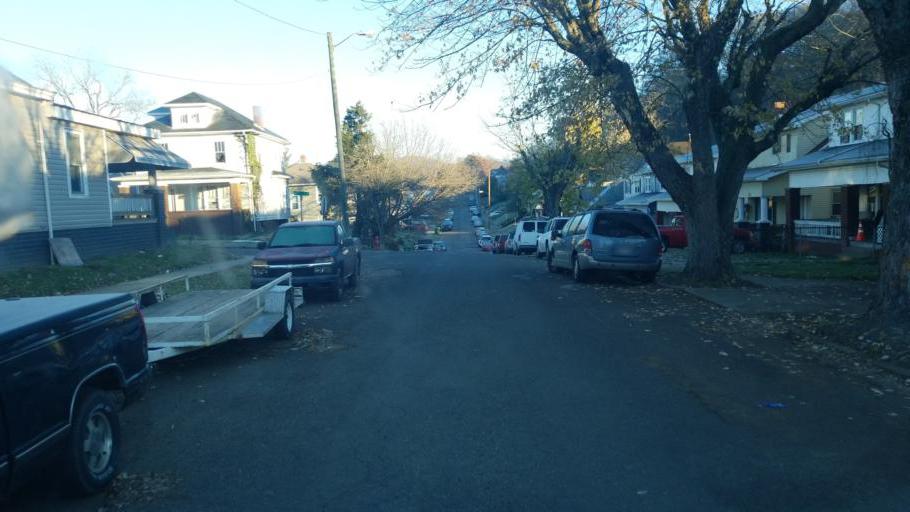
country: US
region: Ohio
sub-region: Scioto County
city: Portsmouth
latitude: 38.7447
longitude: -82.9729
